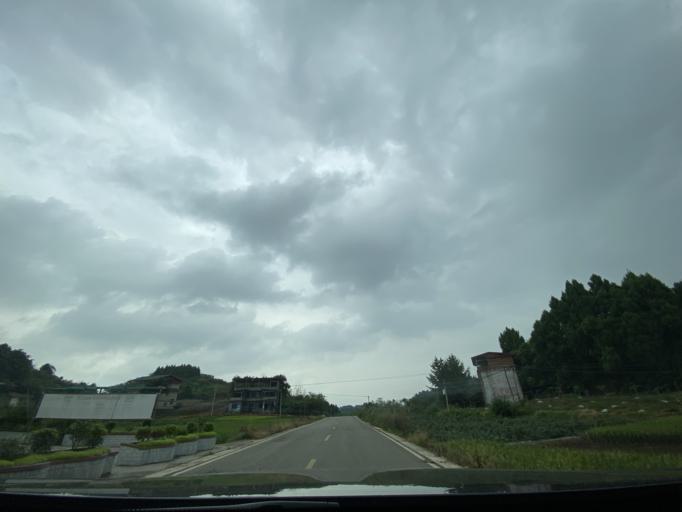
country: CN
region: Sichuan
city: Jiancheng
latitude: 30.5341
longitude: 104.5356
